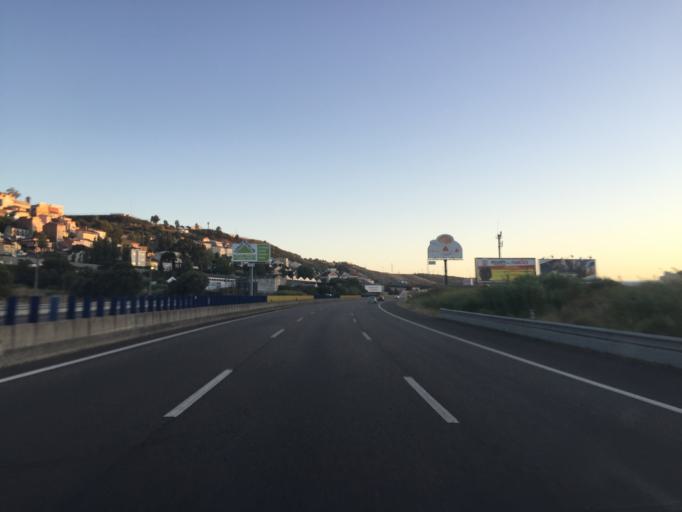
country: PT
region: Lisbon
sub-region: Odivelas
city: Povoa de Santo Adriao
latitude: 38.7998
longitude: -9.1555
